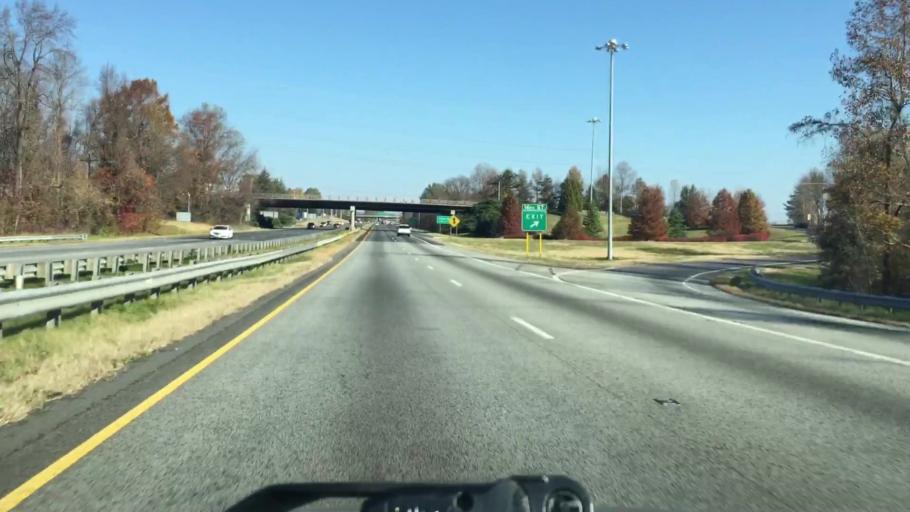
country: US
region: North Carolina
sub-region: Guilford County
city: Greensboro
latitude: 36.1047
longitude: -79.7618
